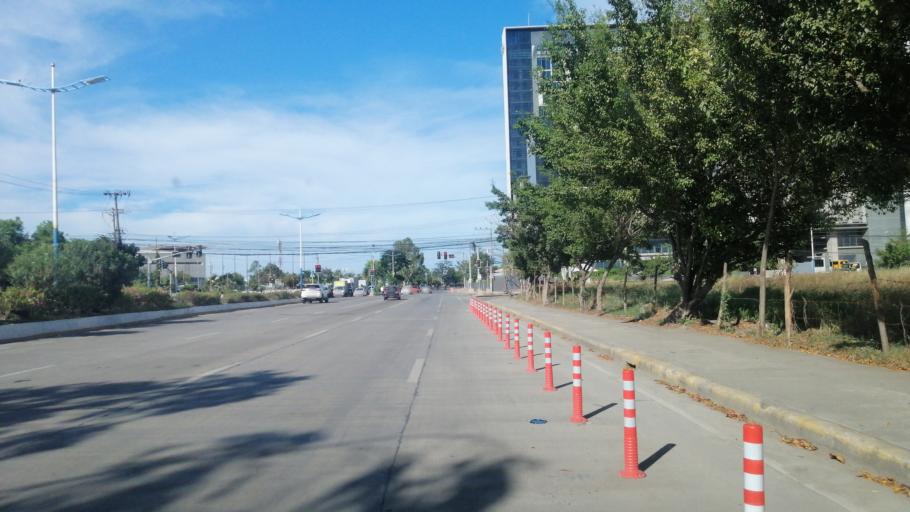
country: PH
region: Central Visayas
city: Mandaue City
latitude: 10.3243
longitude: 123.9355
